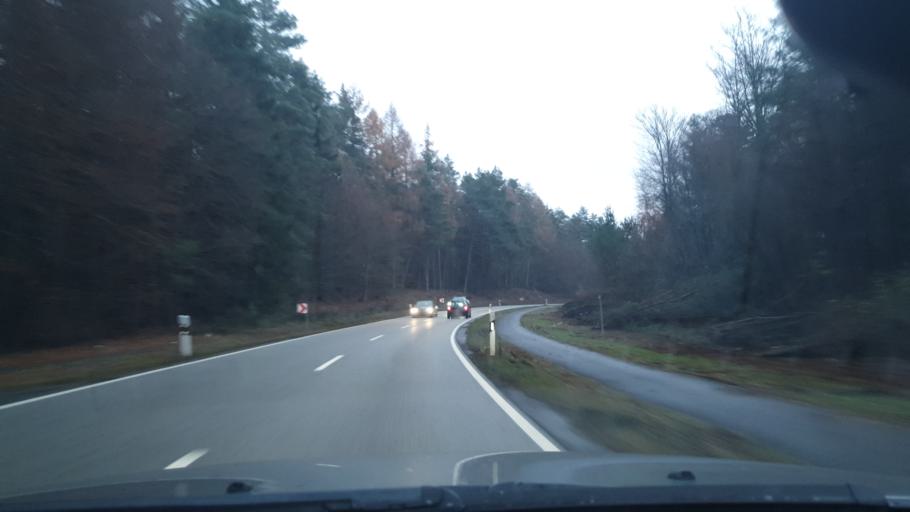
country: DE
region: Rheinland-Pfalz
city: Krickenbach
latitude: 49.3871
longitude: 7.6686
